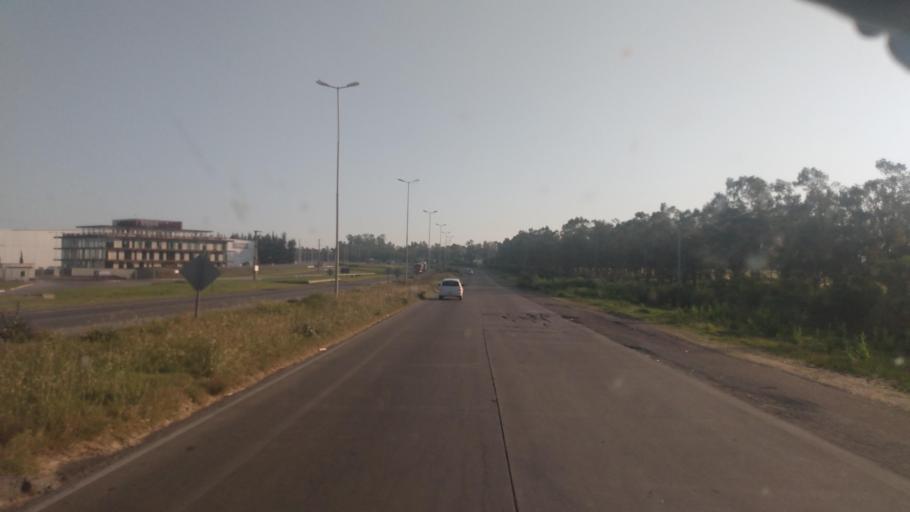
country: AR
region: Buenos Aires
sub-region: Partido de Campana
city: Campana
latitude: -34.2391
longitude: -58.9641
